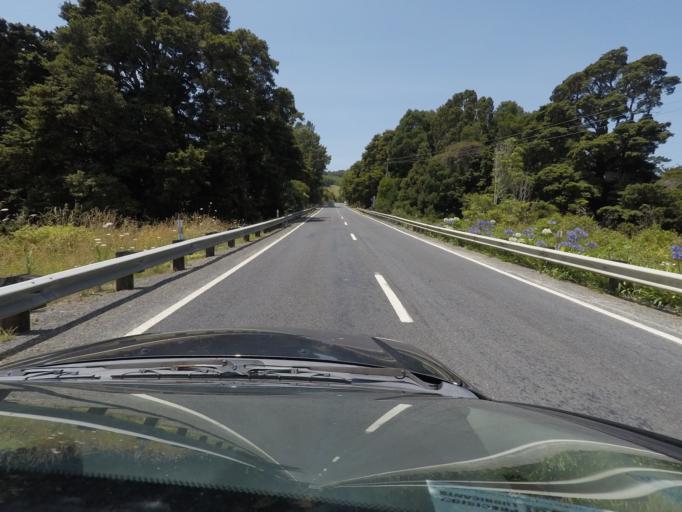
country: NZ
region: Auckland
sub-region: Auckland
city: Warkworth
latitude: -36.3213
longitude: 174.7318
